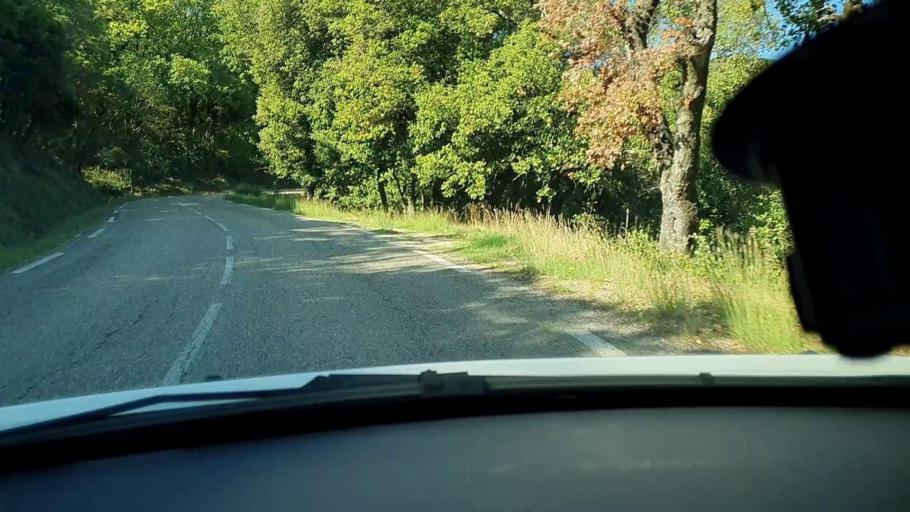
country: FR
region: Languedoc-Roussillon
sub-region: Departement du Gard
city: Saint-Paulet-de-Caisson
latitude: 44.2365
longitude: 4.5544
